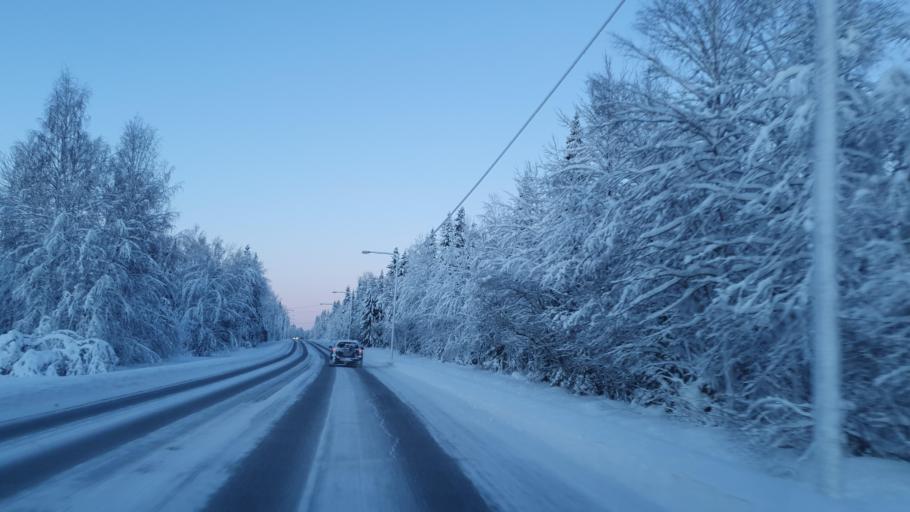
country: FI
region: Lapland
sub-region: Kemi-Tornio
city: Tornio
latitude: 65.9978
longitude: 24.0739
